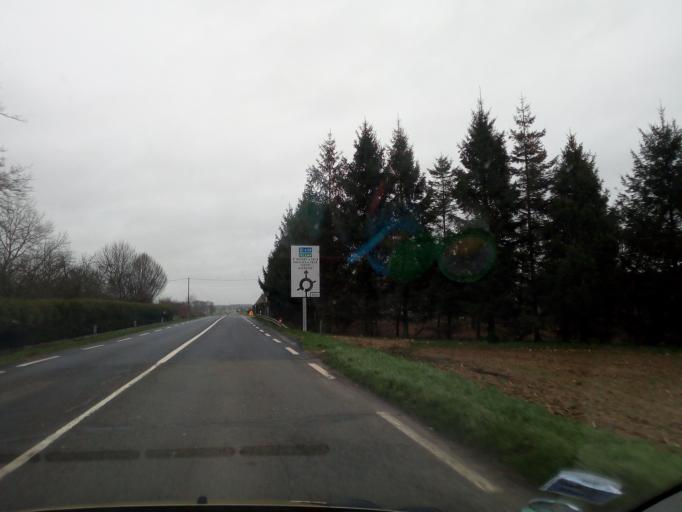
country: FR
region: Haute-Normandie
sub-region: Departement de la Seine-Maritime
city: Auzebosc
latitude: 49.5829
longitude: 0.7311
